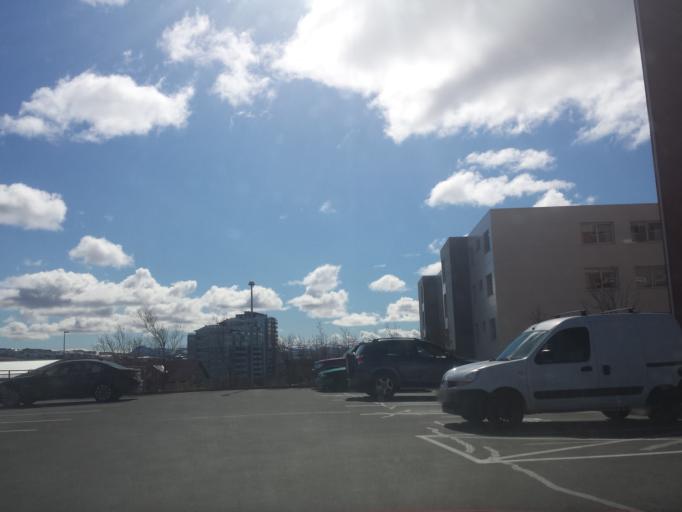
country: IS
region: Capital Region
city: Reykjavik
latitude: 64.0917
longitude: -21.8460
